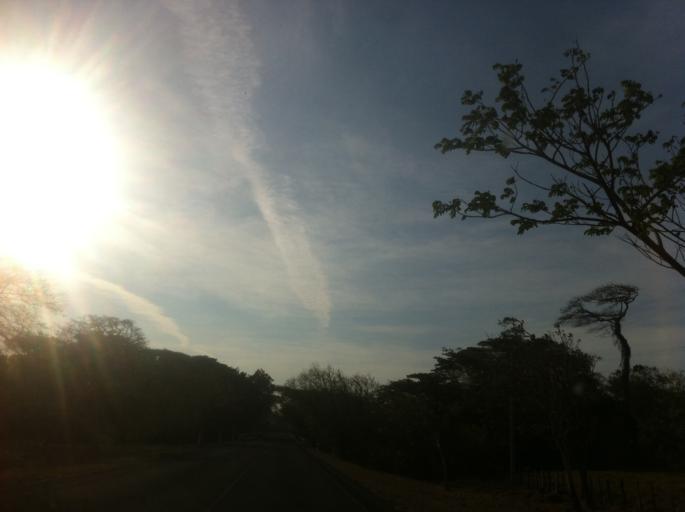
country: NI
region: Rivas
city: Cardenas
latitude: 11.2804
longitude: -85.6686
